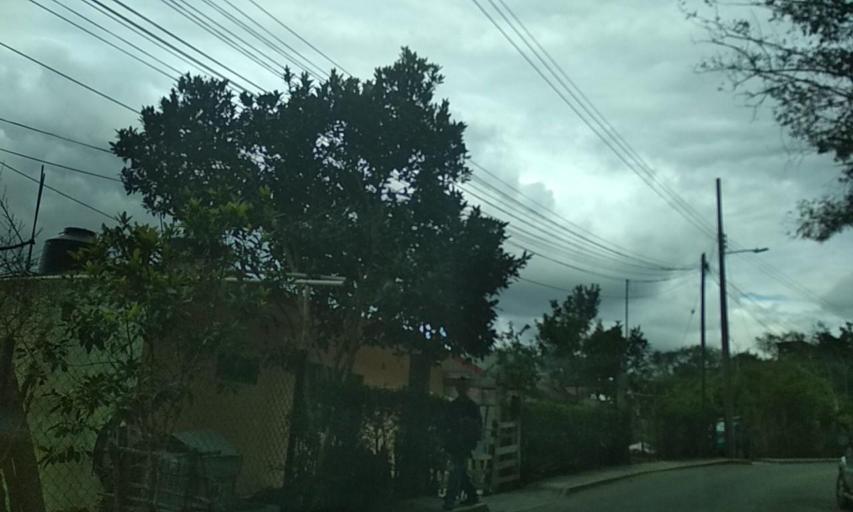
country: MX
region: Veracruz
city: Papantla de Olarte
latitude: 20.4589
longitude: -97.3187
